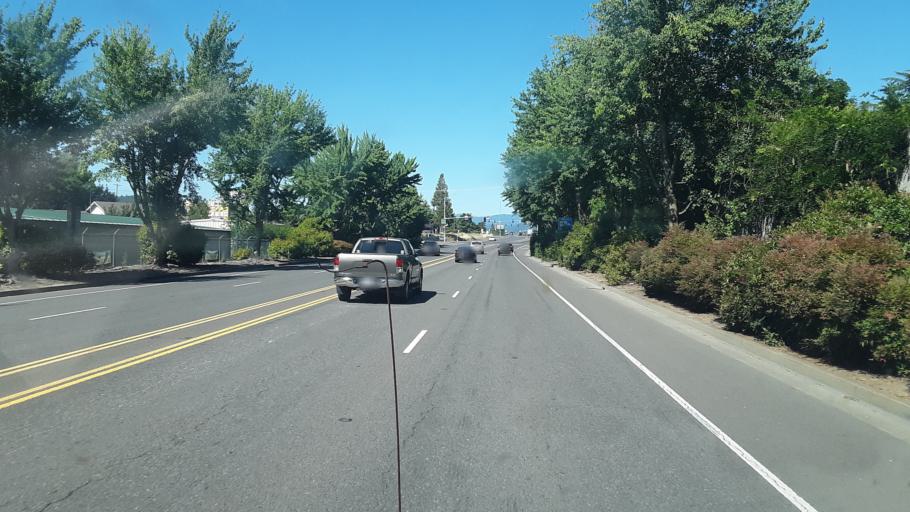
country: US
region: Oregon
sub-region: Josephine County
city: Grants Pass
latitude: 42.4259
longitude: -123.3261
